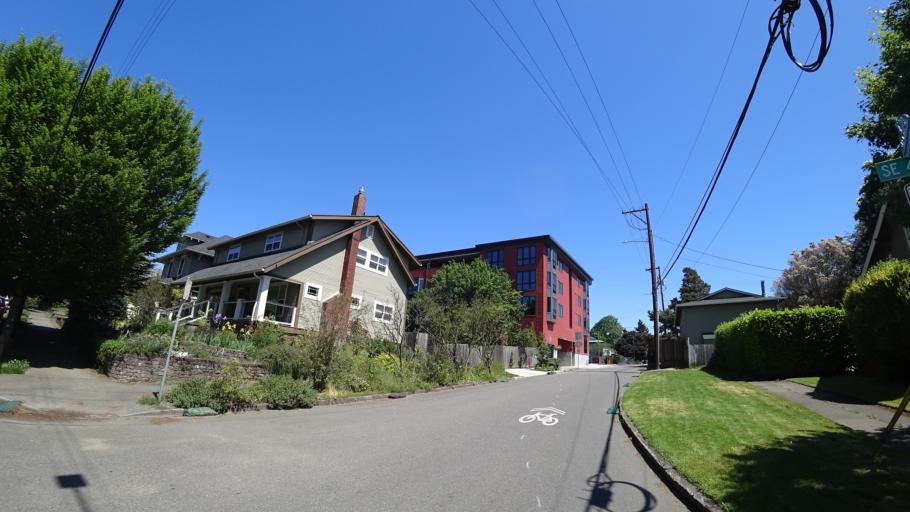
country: US
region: Oregon
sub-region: Multnomah County
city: Lents
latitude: 45.5034
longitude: -122.6120
